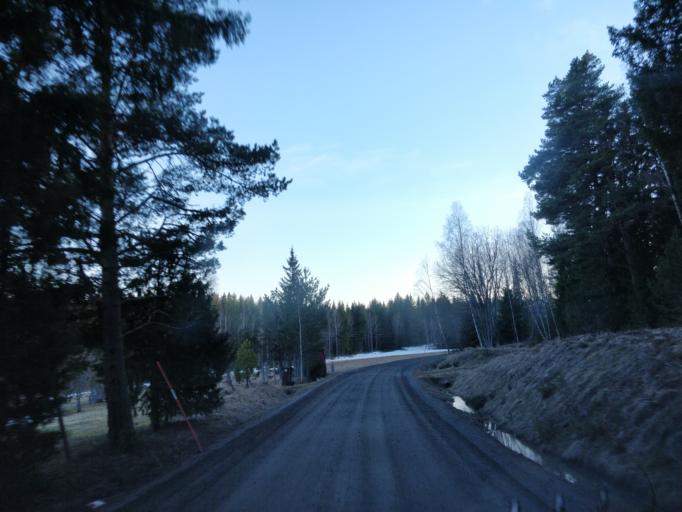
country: SE
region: Uppsala
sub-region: Enkopings Kommun
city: Orsundsbro
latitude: 59.8300
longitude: 17.1818
